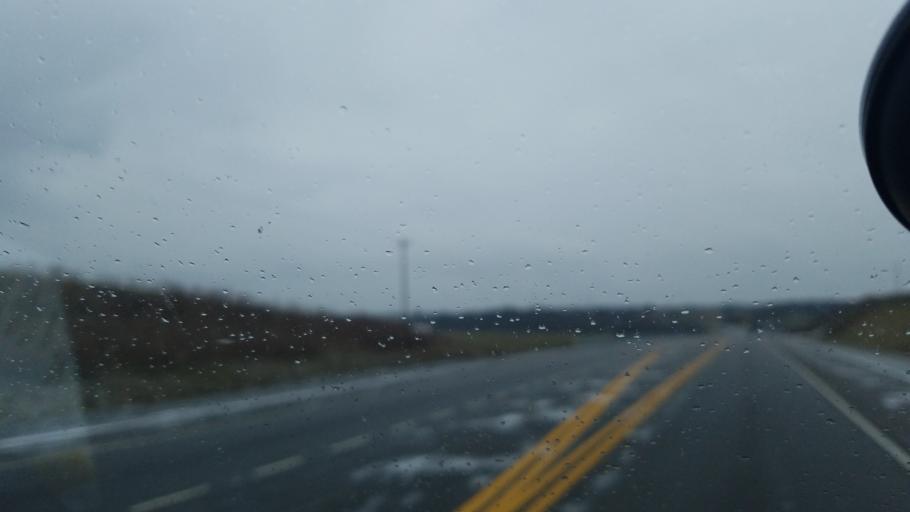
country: US
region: Kentucky
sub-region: Fleming County
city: Flemingsburg
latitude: 38.4417
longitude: -83.7356
